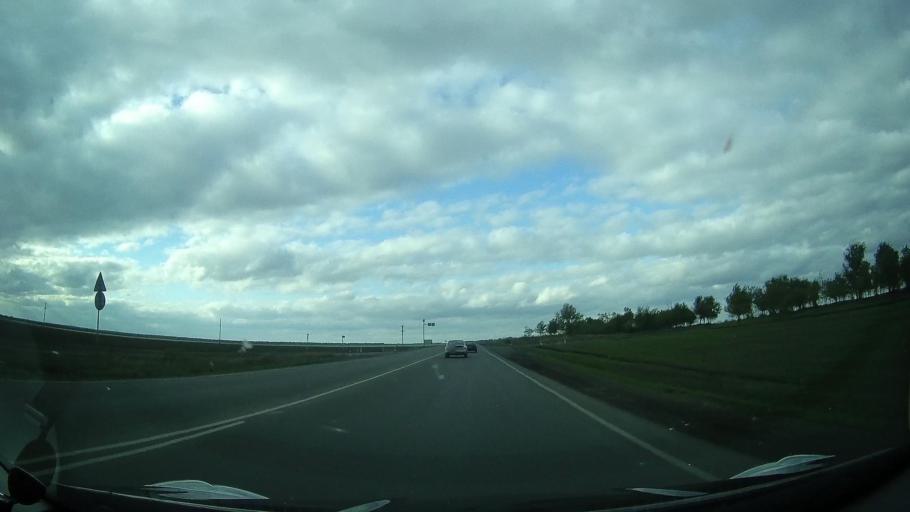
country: RU
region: Rostov
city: Kagal'nitskaya
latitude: 46.8924
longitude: 40.1299
